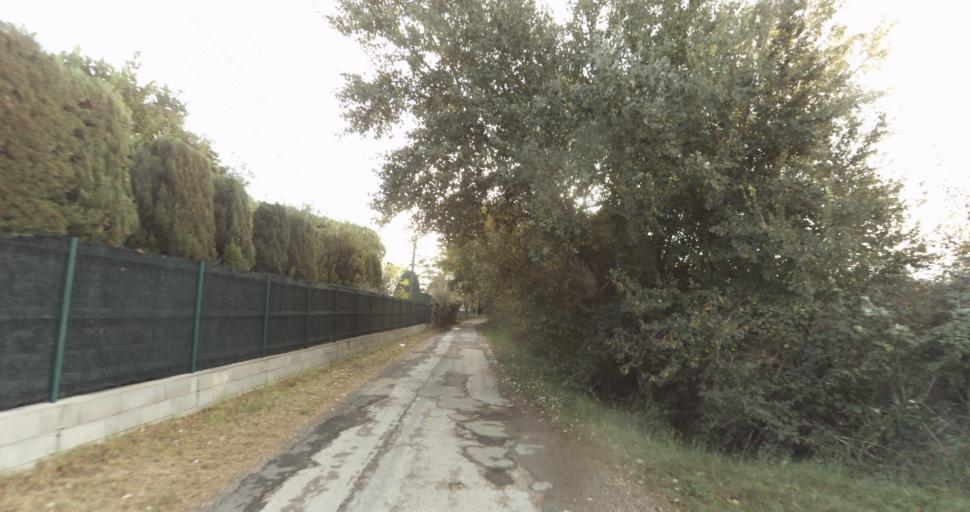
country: FR
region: Languedoc-Roussillon
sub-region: Departement du Gard
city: Aigues-Mortes
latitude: 43.5626
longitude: 4.2073
